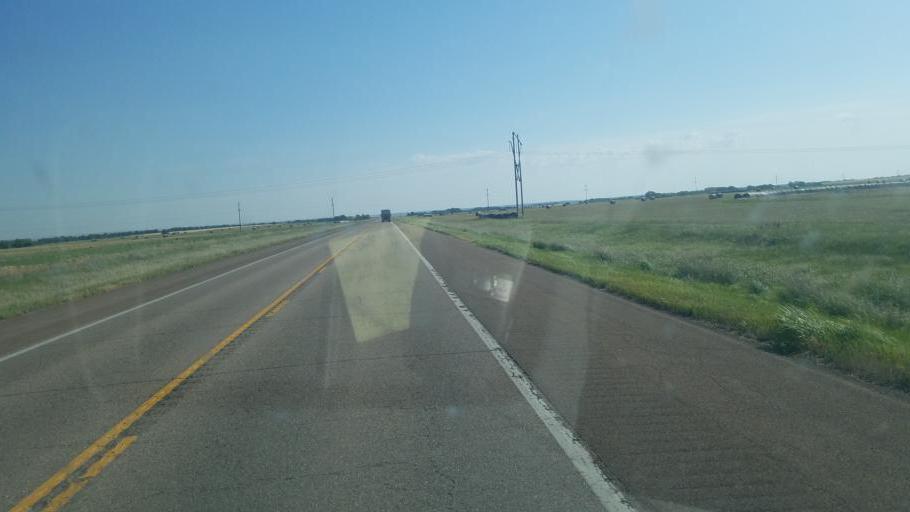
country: US
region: Kansas
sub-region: Barton County
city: Great Bend
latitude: 38.3877
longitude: -98.6789
